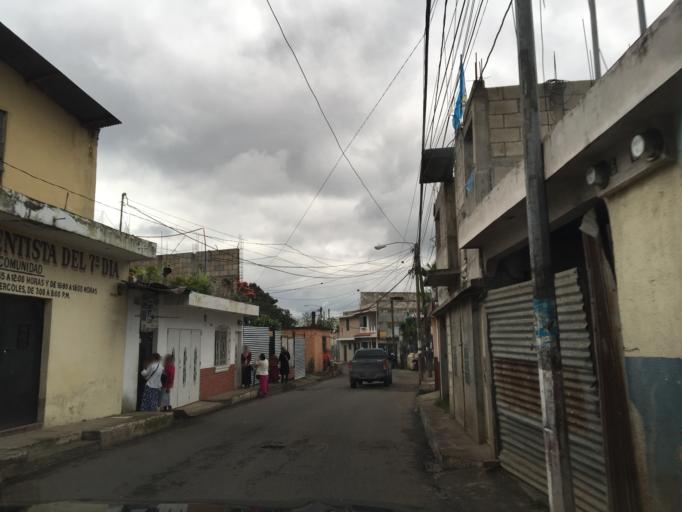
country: GT
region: Guatemala
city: Mixco
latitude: 14.6217
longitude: -90.5862
